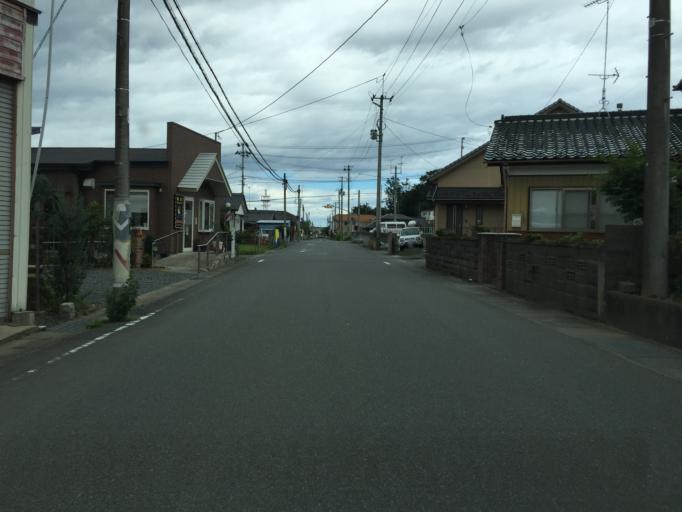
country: JP
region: Fukushima
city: Namie
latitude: 37.6255
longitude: 140.9615
